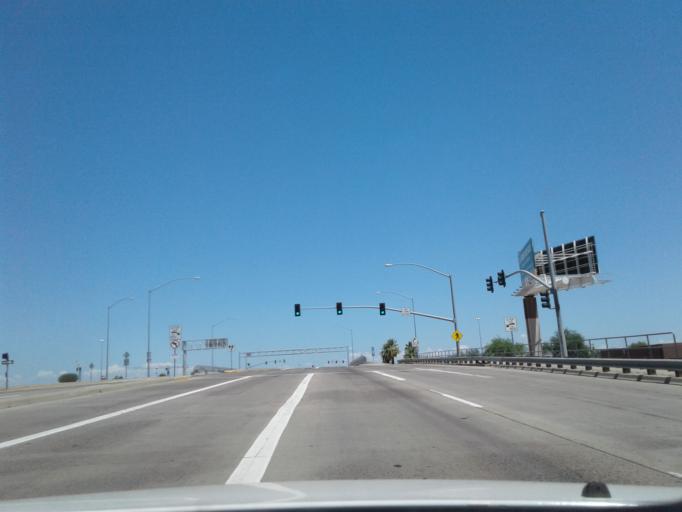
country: US
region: Arizona
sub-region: Maricopa County
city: Guadalupe
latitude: 33.4090
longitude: -111.9953
